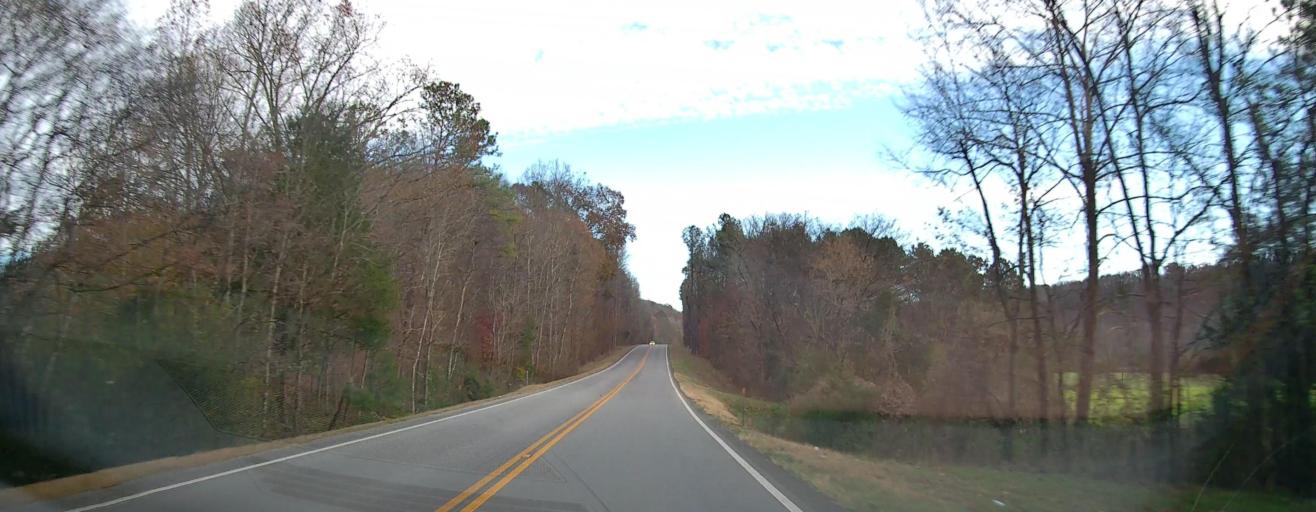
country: US
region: Alabama
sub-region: Marshall County
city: Arab
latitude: 34.3683
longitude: -86.6385
